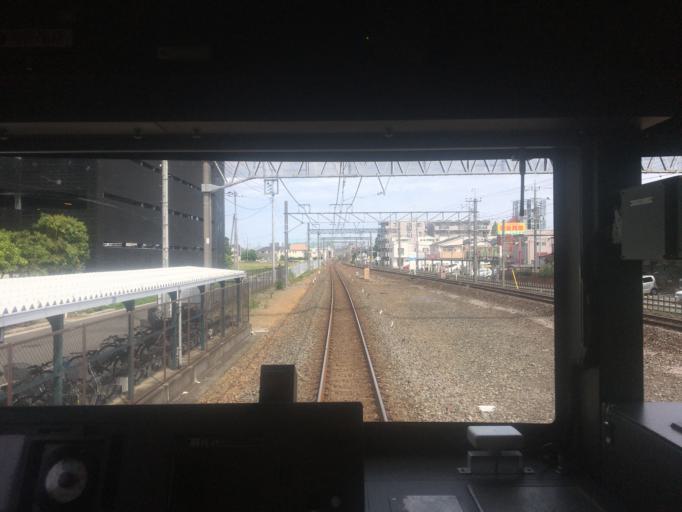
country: JP
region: Saitama
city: Sakado
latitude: 35.9498
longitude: 139.4077
